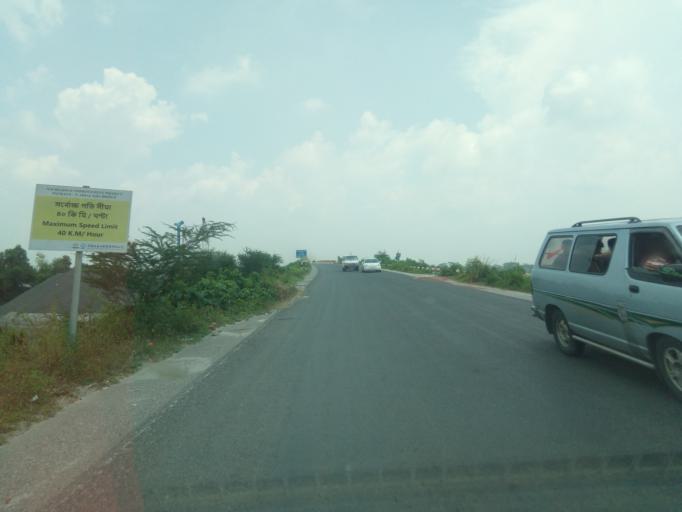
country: BD
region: Dhaka
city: Char Bhadrasan
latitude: 23.3780
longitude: 90.1125
